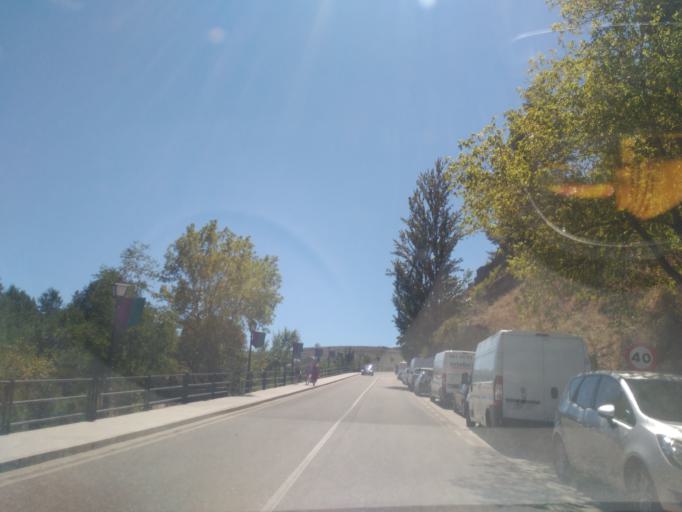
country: ES
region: Castille and Leon
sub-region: Provincia de Zamora
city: Puebla de Sanabria
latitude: 42.0551
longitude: -6.6329
